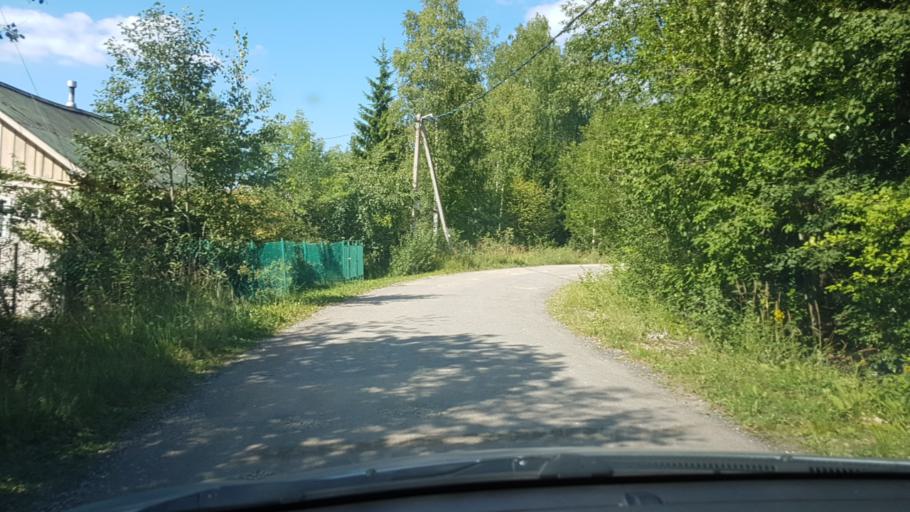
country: RU
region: Leningrad
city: Vyritsa
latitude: 59.4486
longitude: 30.2941
